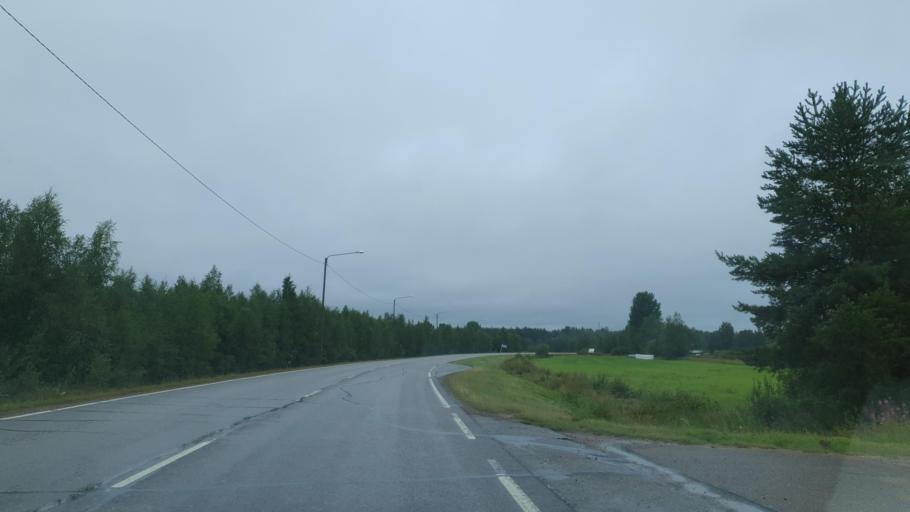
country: FI
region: Lapland
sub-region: Itae-Lappi
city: Kemijaervi
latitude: 66.6939
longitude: 27.5759
